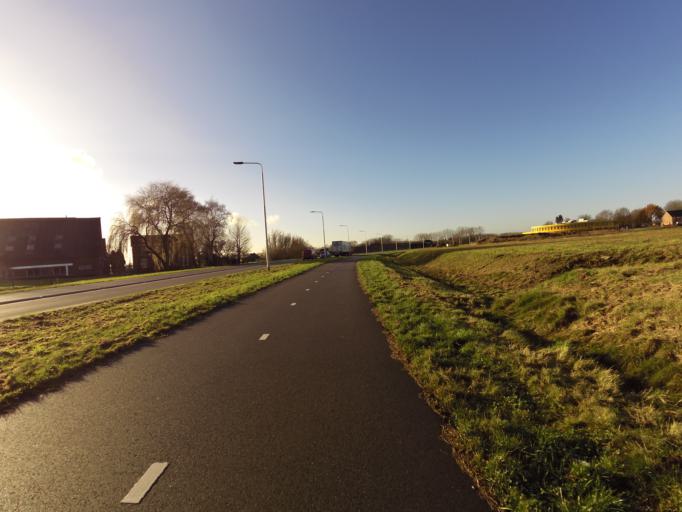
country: NL
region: Gelderland
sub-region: Gemeente Zevenaar
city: Zevenaar
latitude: 51.9278
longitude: 6.1259
